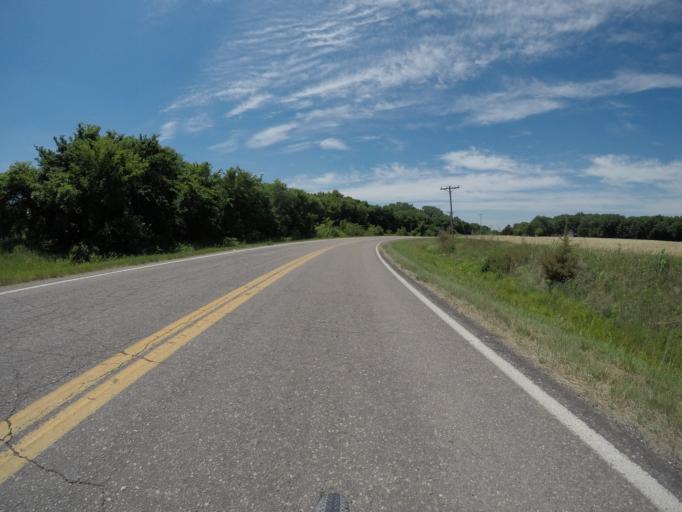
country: US
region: Kansas
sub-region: Wabaunsee County
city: Alma
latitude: 39.0480
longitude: -96.2473
